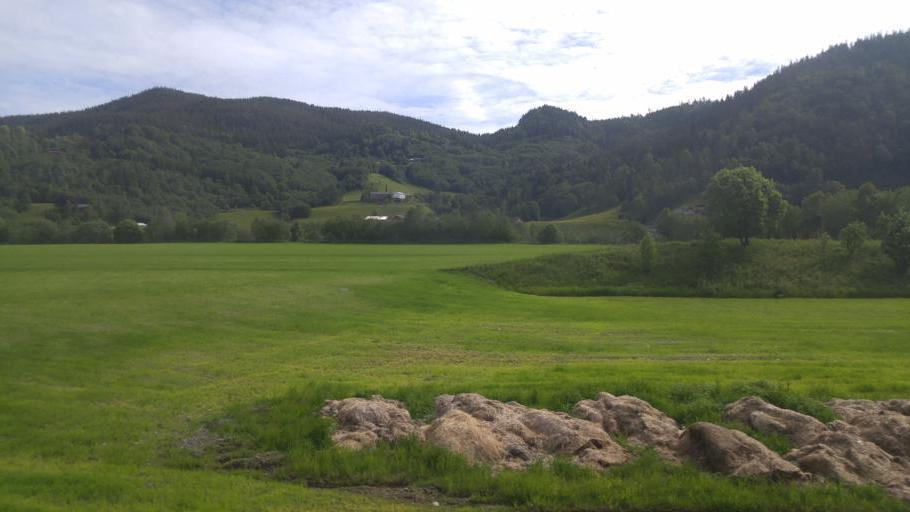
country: NO
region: Sor-Trondelag
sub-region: Midtre Gauldal
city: Storen
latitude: 63.0879
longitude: 10.2423
